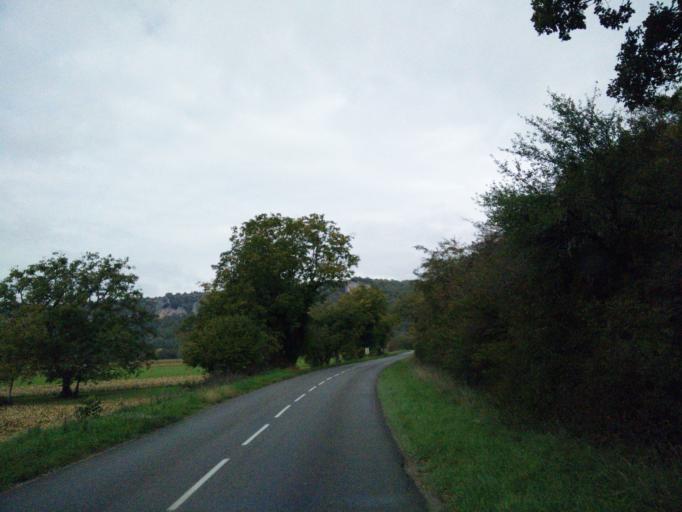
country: FR
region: Midi-Pyrenees
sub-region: Departement du Lot
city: Lalbenque
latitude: 44.4719
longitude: 1.5873
